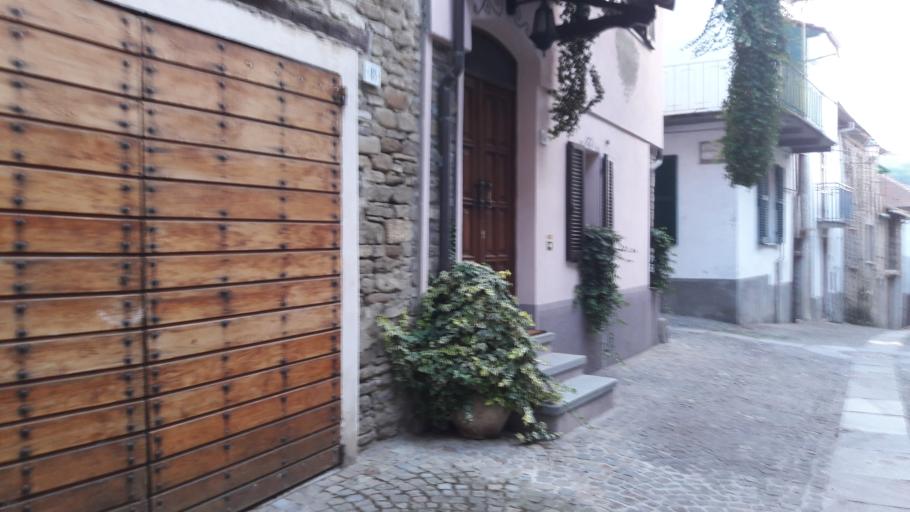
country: IT
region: Piedmont
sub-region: Provincia di Asti
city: Monastero Bormida
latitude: 44.6490
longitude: 8.3246
